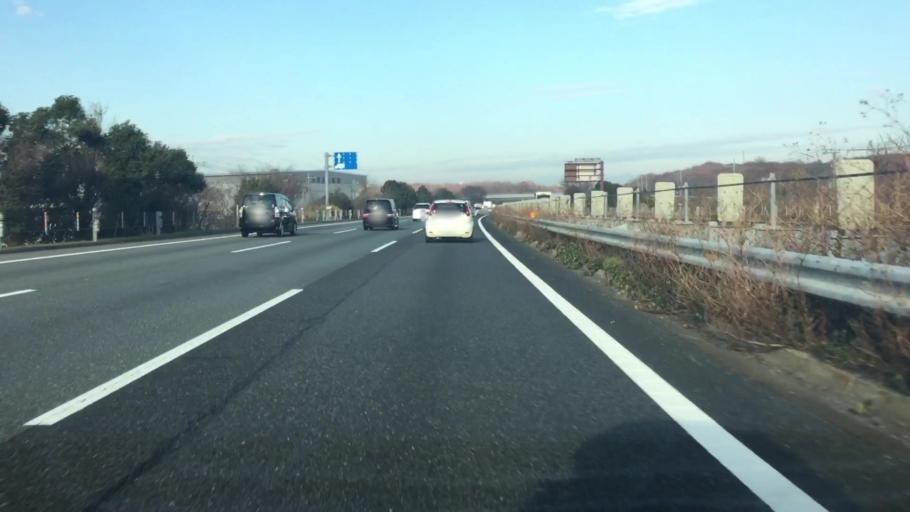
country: JP
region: Saitama
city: Honjo
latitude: 36.2039
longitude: 139.1767
